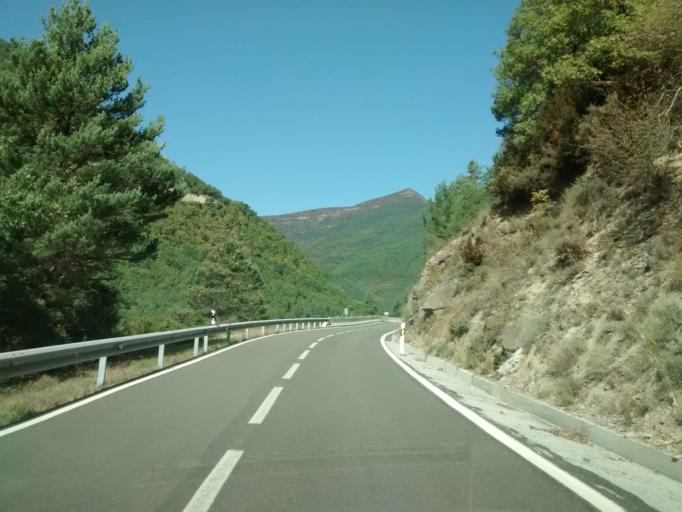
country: ES
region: Aragon
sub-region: Provincia de Huesca
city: Fiscal
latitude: 42.5242
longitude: -0.1338
